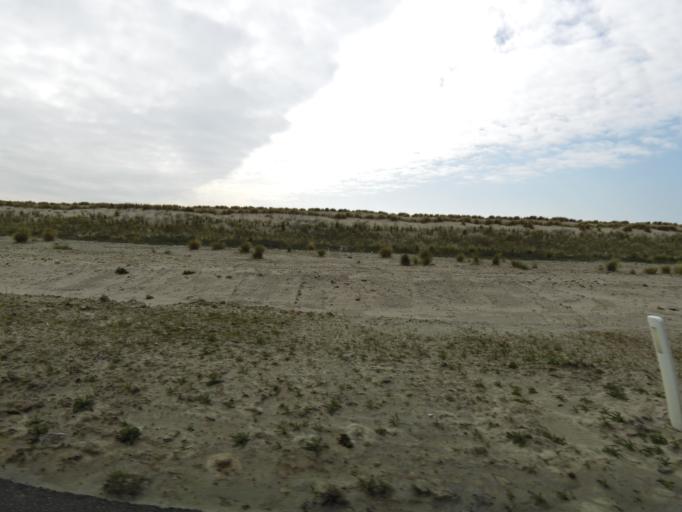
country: NL
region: South Holland
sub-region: Gemeente Goeree-Overflakkee
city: Goedereede
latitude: 51.9545
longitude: 3.9661
